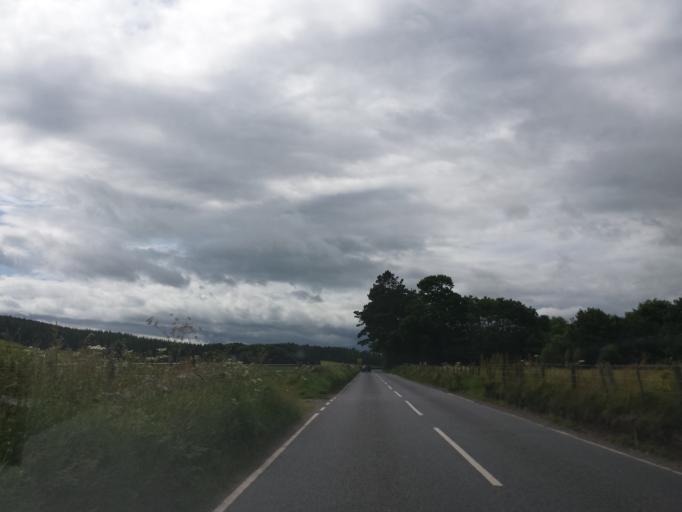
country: GB
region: Scotland
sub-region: Highland
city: Nairn
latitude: 57.5249
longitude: -3.9521
